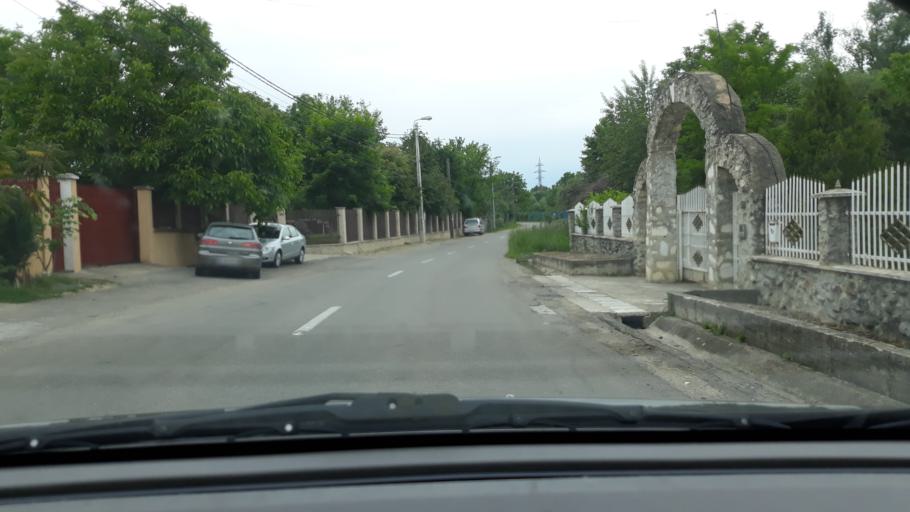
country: RO
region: Bihor
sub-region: Comuna Sanmartin
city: Sanmartin
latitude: 47.0514
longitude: 21.9814
